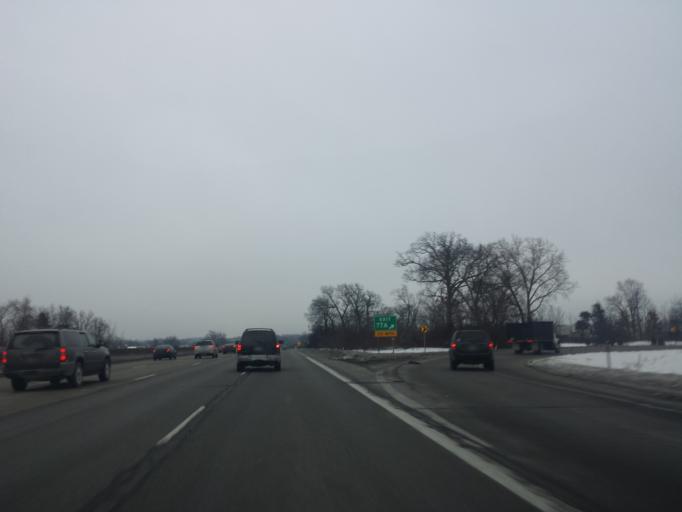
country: US
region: Michigan
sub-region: Oakland County
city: Auburn Hills
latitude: 42.6410
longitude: -83.2387
